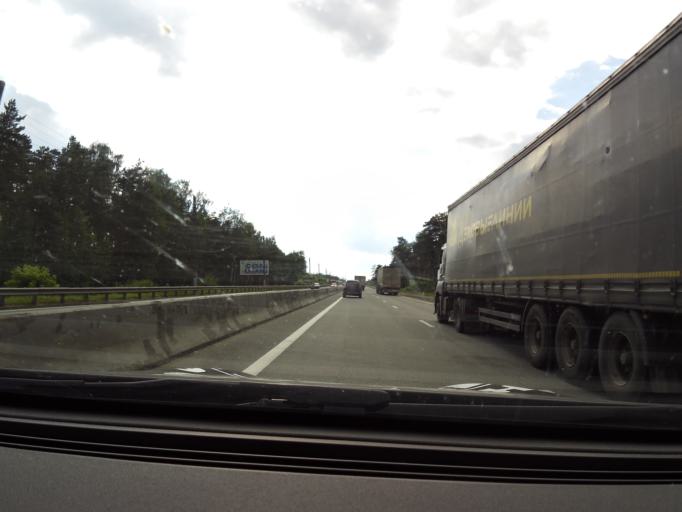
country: RU
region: Nizjnij Novgorod
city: Dzerzhinsk
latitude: 56.2981
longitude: 43.4692
